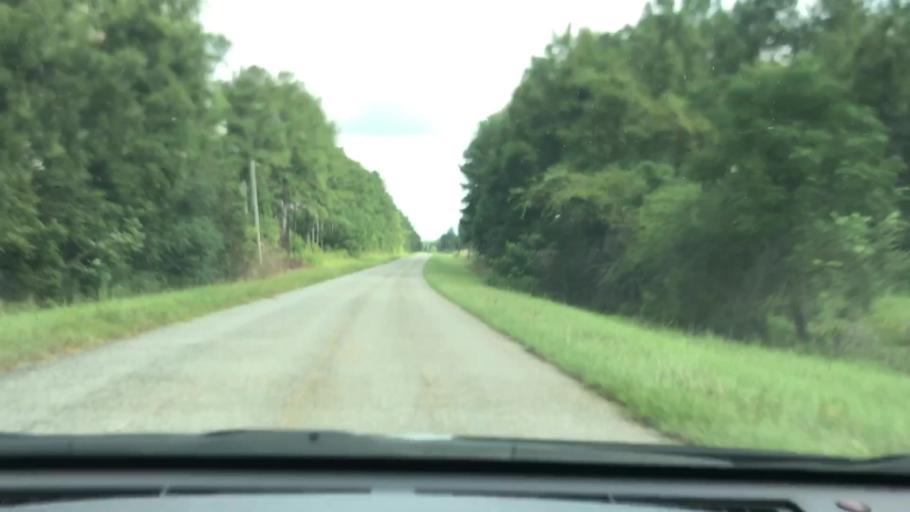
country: US
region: Georgia
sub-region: Jefferson County
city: Wadley
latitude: 32.8030
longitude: -82.3681
